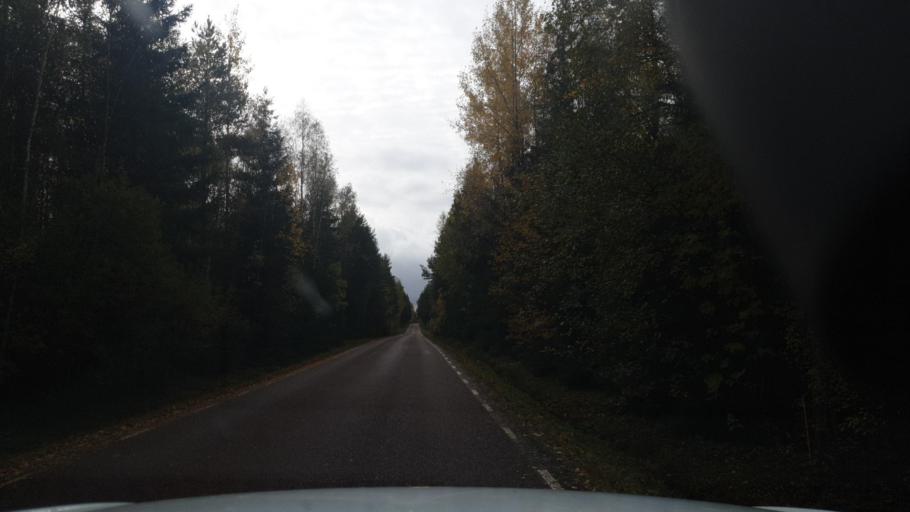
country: SE
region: Vaermland
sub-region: Karlstads Kommun
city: Edsvalla
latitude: 59.5042
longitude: 13.1094
